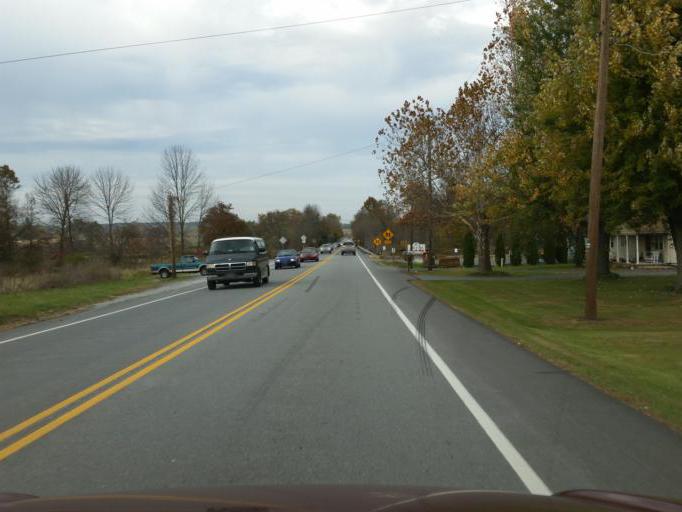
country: US
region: Pennsylvania
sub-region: Lancaster County
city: Elizabethtown
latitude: 40.1859
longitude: -76.6018
